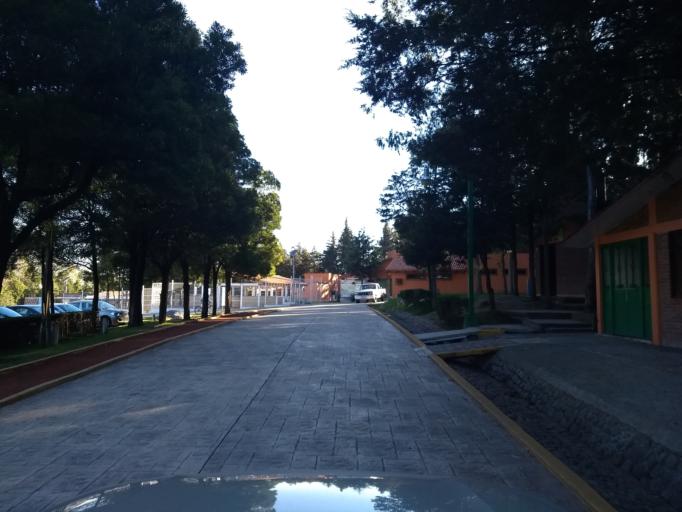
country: MX
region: Mexico
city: San Marcos Yachihuacaltepec
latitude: 19.3112
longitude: -99.6859
